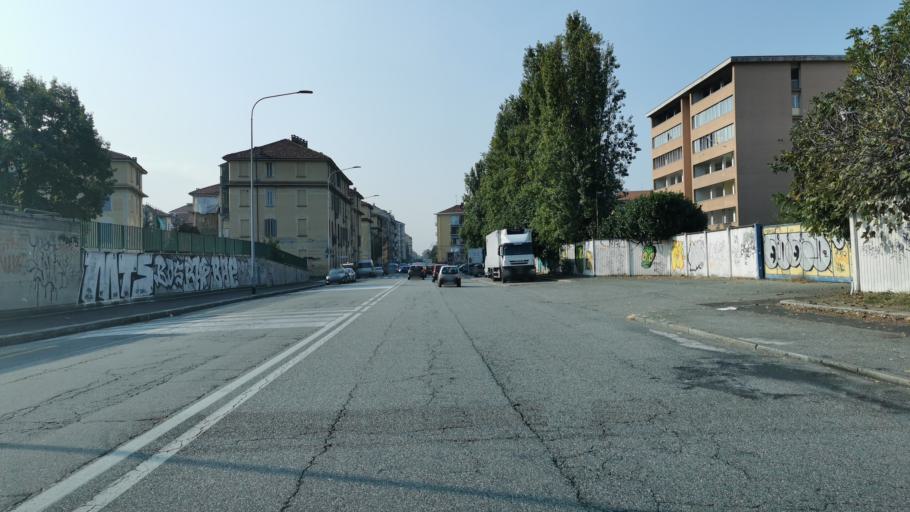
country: IT
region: Piedmont
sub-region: Provincia di Torino
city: Turin
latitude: 45.0982
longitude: 7.6898
